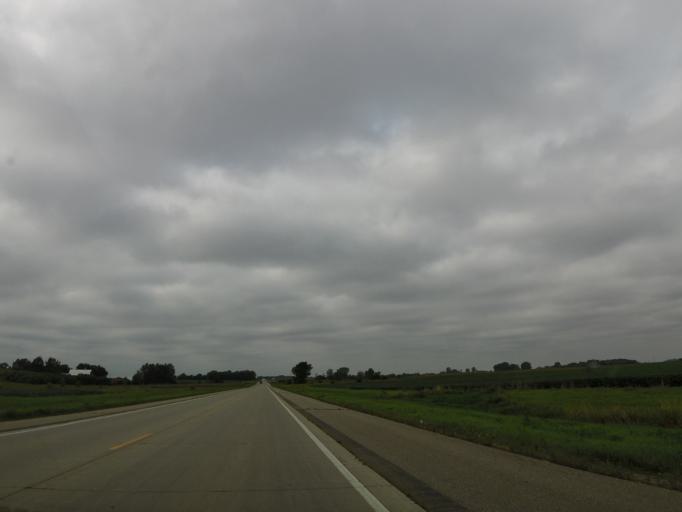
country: US
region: Minnesota
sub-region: Renville County
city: Renville
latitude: 44.7890
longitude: -95.1106
